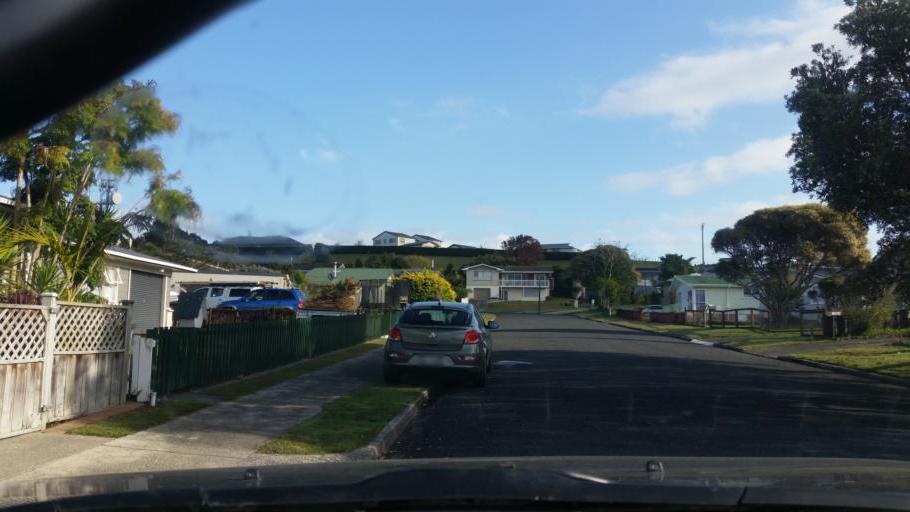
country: NZ
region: Northland
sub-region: Kaipara District
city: Dargaville
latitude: -35.9292
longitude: 173.8563
